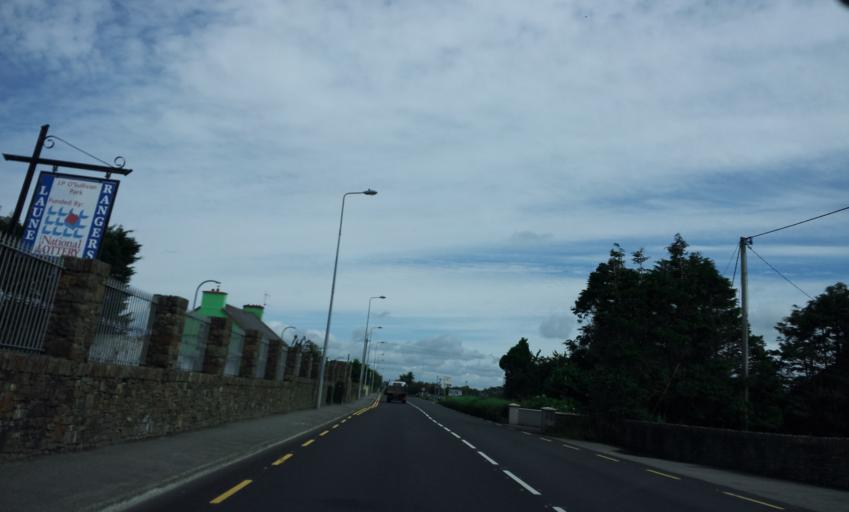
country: IE
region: Munster
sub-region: Ciarrai
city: Killorglin
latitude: 52.1043
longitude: -9.8002
